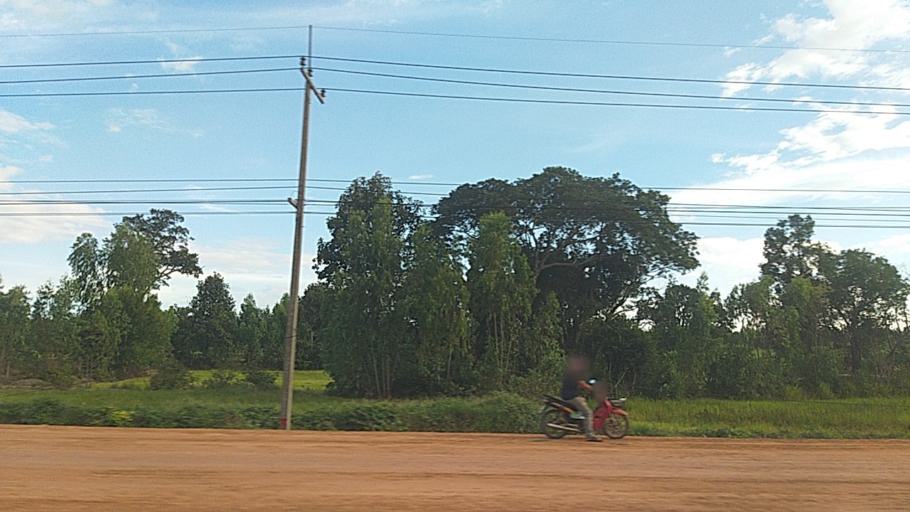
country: TH
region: Surin
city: Kap Choeng
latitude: 14.4586
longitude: 103.6679
